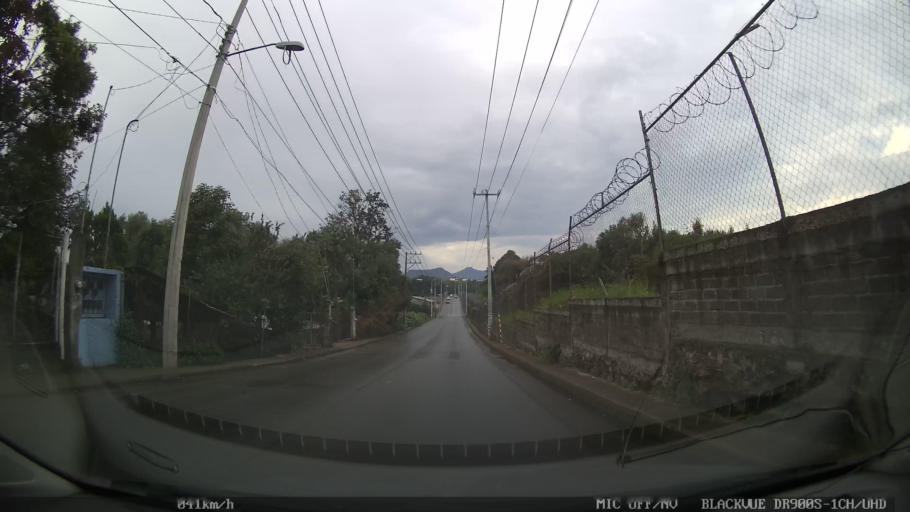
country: MX
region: Michoacan
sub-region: Uruapan
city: Santa Rosa (Santa Barbara)
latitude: 19.3832
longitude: -102.0469
